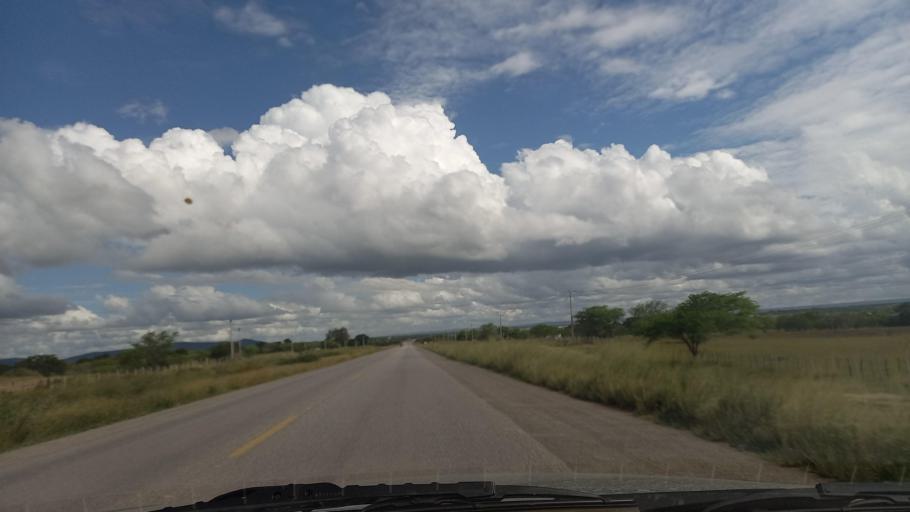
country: BR
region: Pernambuco
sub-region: Cachoeirinha
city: Cachoeirinha
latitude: -8.4705
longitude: -36.2200
